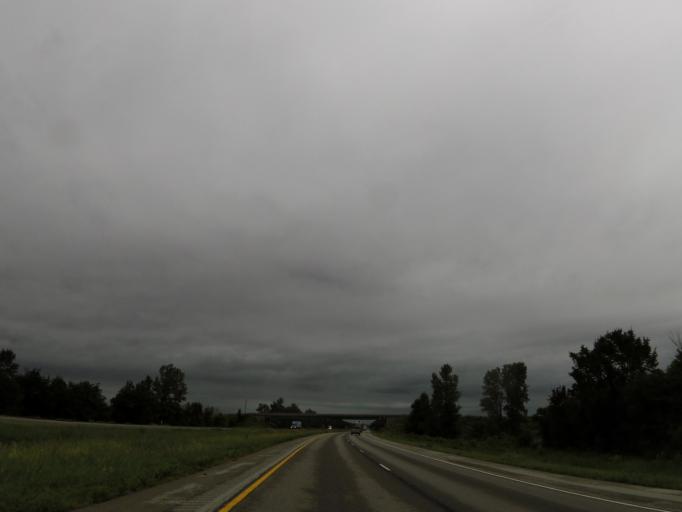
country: US
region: Illinois
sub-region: Massac County
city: Metropolis
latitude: 37.2736
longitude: -88.7436
